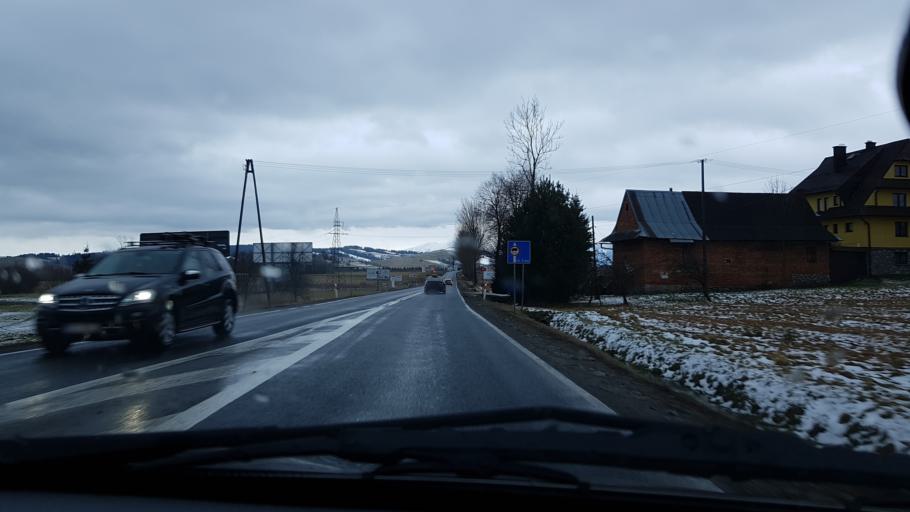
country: PL
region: Lesser Poland Voivodeship
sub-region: Powiat tatrzanski
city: Bialka Tatrzanska
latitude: 49.4202
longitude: 20.0926
